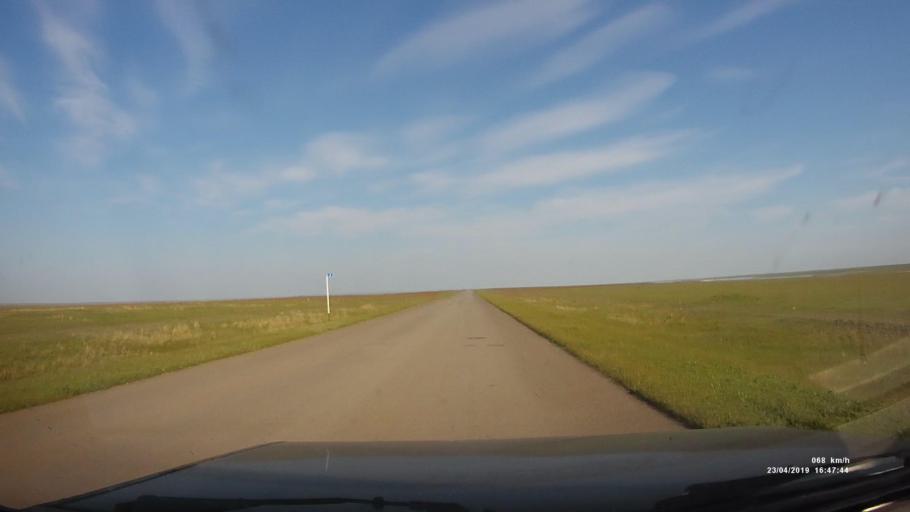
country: RU
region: Kalmykiya
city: Priyutnoye
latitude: 46.3376
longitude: 43.2521
